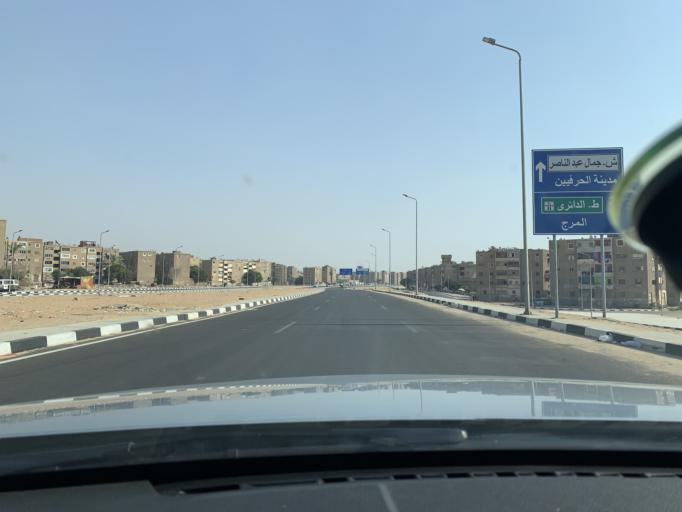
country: EG
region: Muhafazat al Qalyubiyah
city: Al Khankah
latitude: 30.1770
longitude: 31.4148
